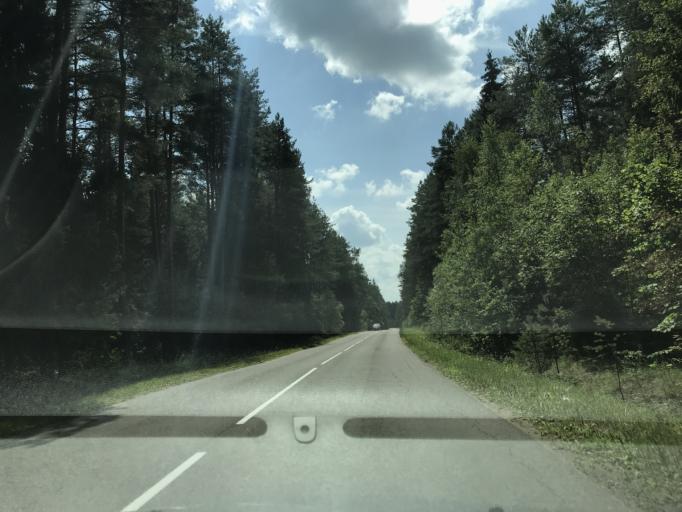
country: BY
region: Minsk
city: Rakaw
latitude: 53.9915
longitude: 26.9912
